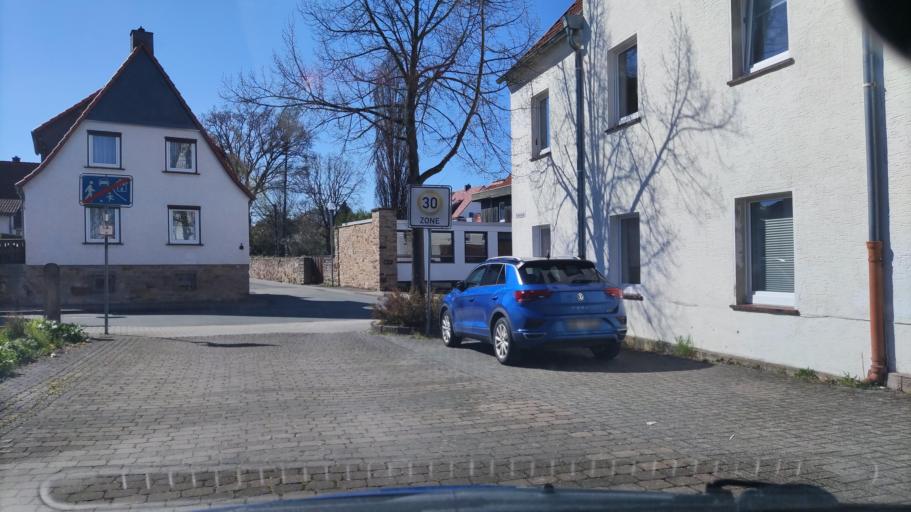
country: DE
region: Hesse
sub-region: Regierungsbezirk Kassel
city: Hofgeismar
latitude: 51.4983
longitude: 9.3825
